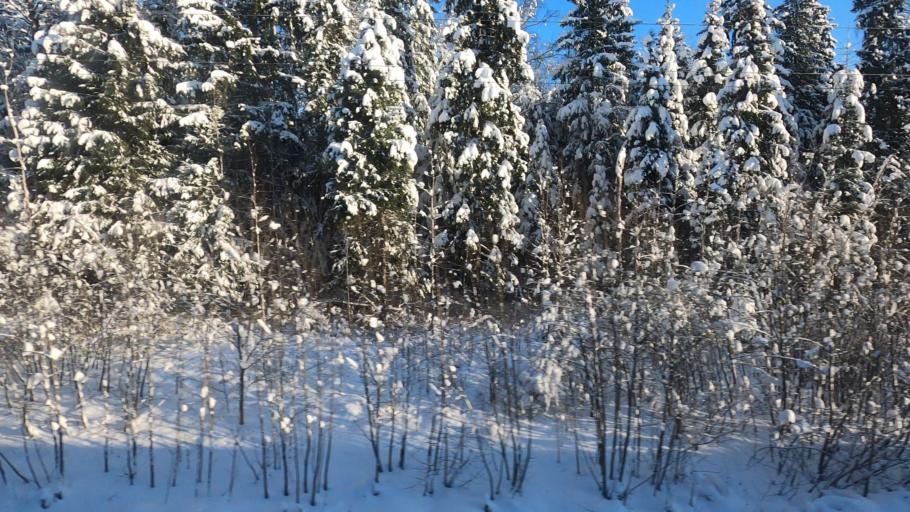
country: RU
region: Moskovskaya
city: Novo-Nikol'skoye
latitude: 56.6175
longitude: 37.5662
